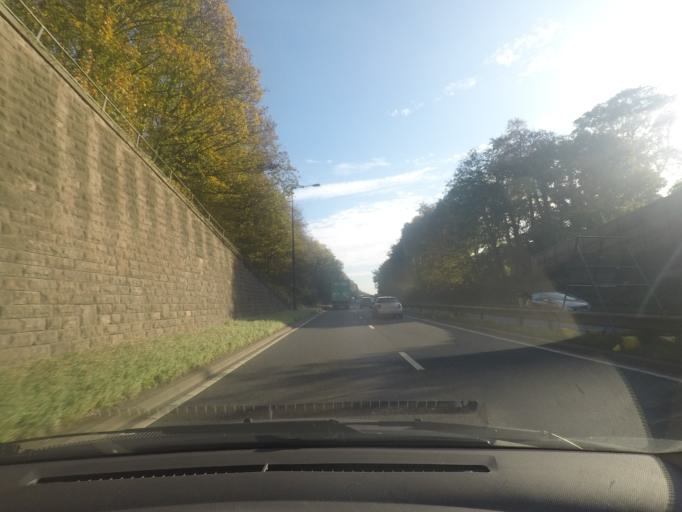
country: GB
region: England
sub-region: East Riding of Yorkshire
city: North Ferriby
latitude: 53.7260
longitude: -0.5070
